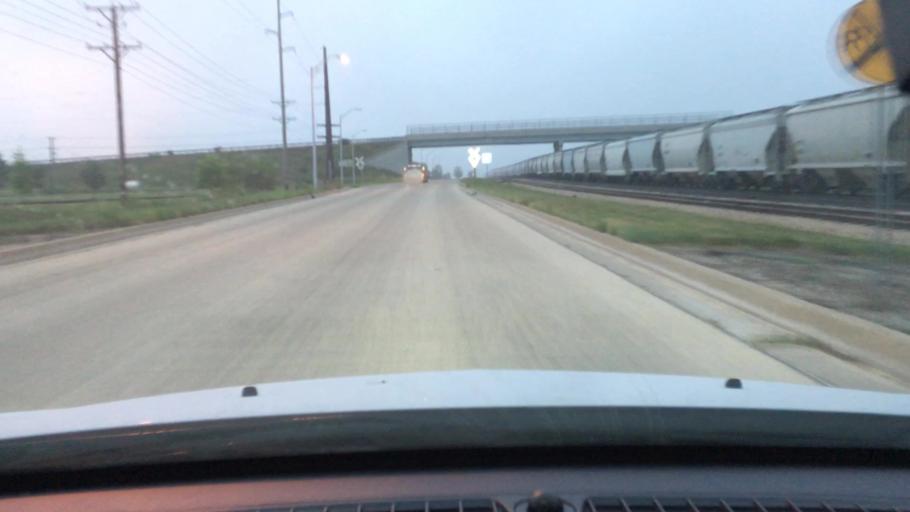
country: US
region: Illinois
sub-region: Ogle County
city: Rochelle
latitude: 41.8997
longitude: -89.0429
